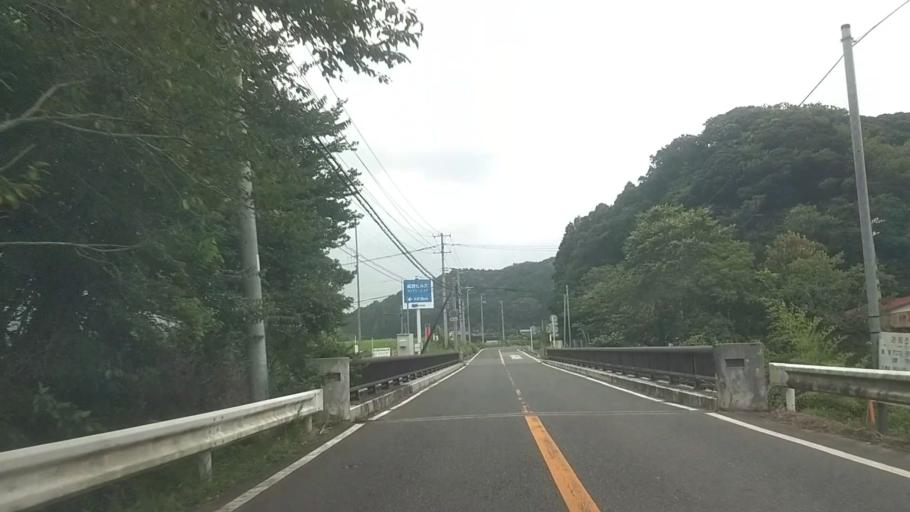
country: JP
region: Chiba
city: Kimitsu
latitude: 35.2179
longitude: 139.9320
